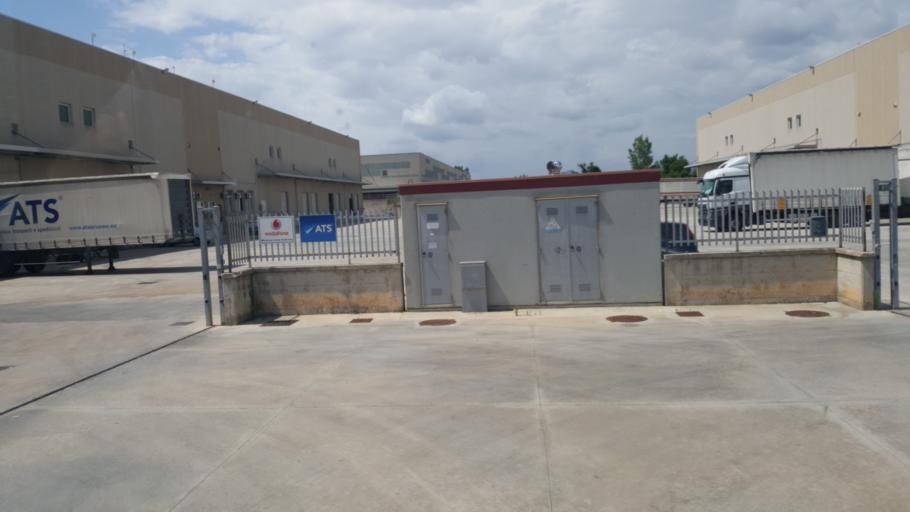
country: IT
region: Campania
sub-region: Provincia di Caserta
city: Maddaloni
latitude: 41.0100
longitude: 14.3632
